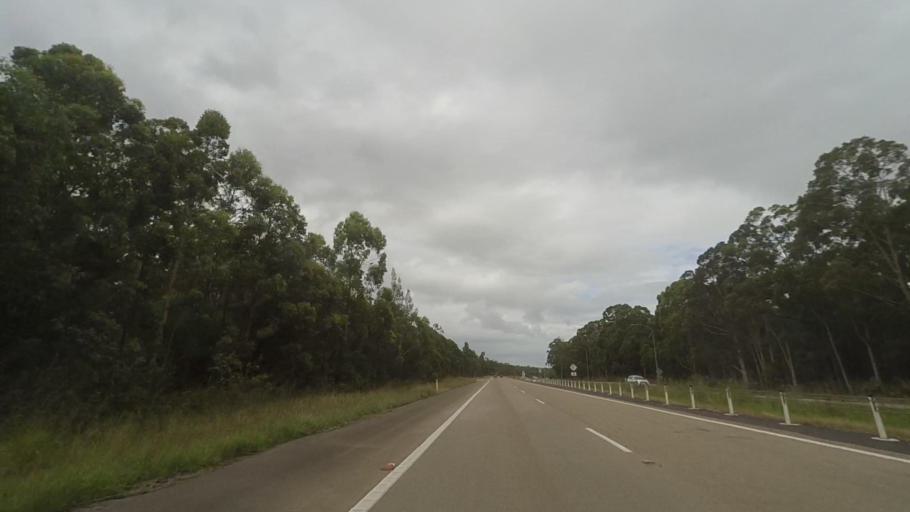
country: AU
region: New South Wales
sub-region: Port Stephens Shire
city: Medowie
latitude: -32.6501
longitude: 151.9097
